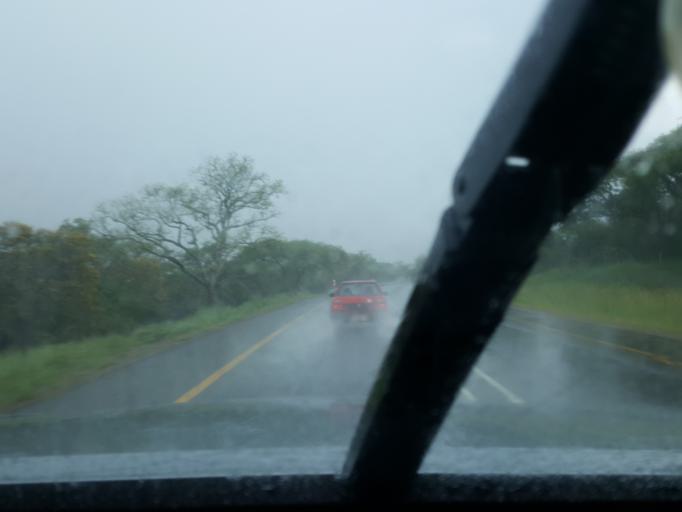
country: ZA
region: Mpumalanga
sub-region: Nkangala District Municipality
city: Belfast
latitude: -25.6052
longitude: 30.4735
